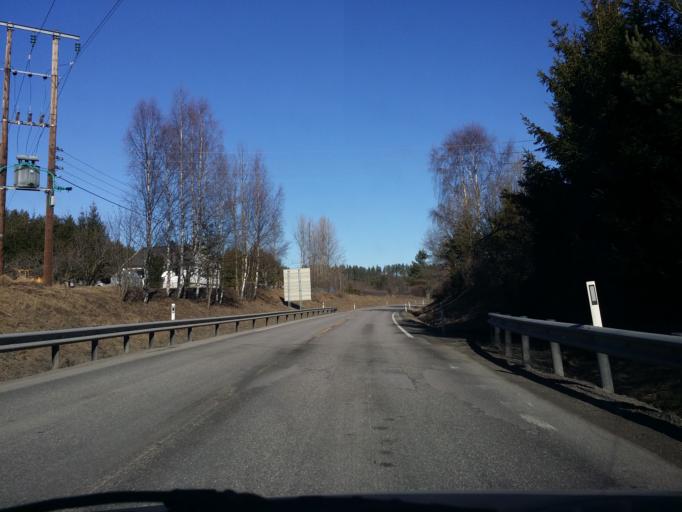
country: NO
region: Buskerud
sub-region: Ringerike
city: Honefoss
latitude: 60.2072
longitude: 10.2570
